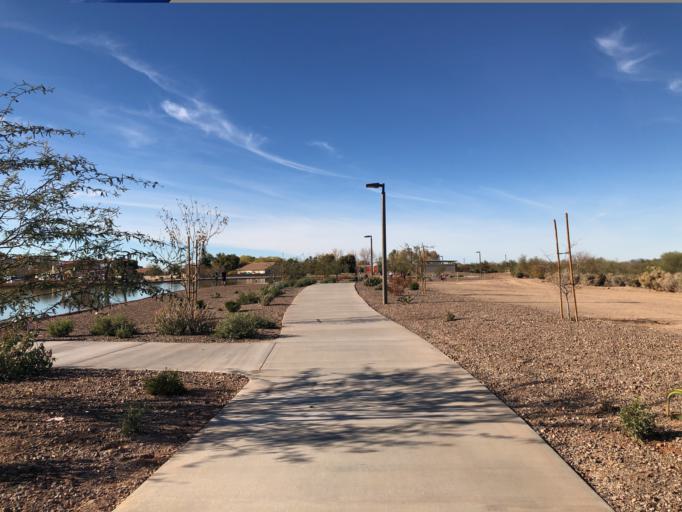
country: US
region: Arizona
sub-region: Maricopa County
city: Queen Creek
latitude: 33.2561
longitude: -111.6588
